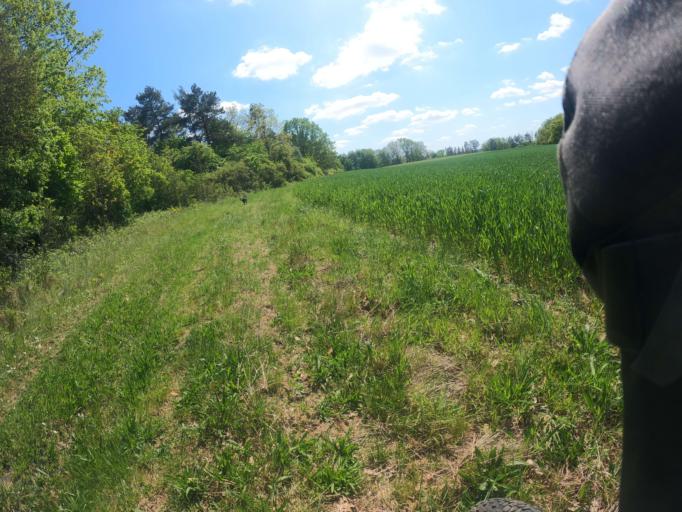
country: PL
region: West Pomeranian Voivodeship
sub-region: Powiat mysliborski
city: Barlinek
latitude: 53.0404
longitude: 15.2224
